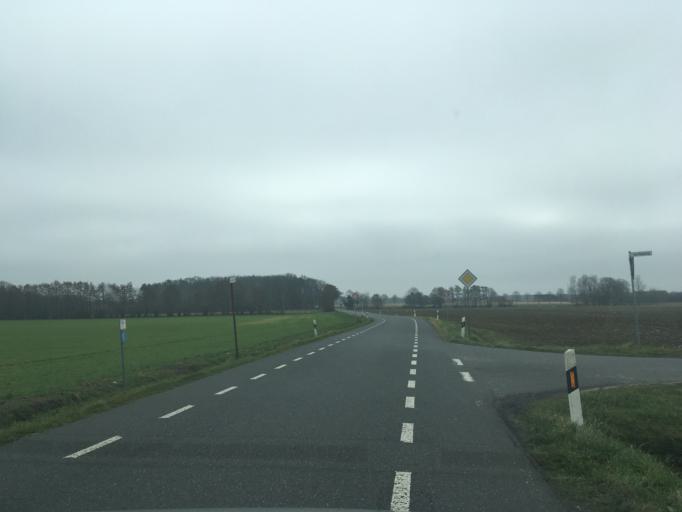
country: DE
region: North Rhine-Westphalia
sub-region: Regierungsbezirk Munster
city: Rhede
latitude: 51.8696
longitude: 6.7278
